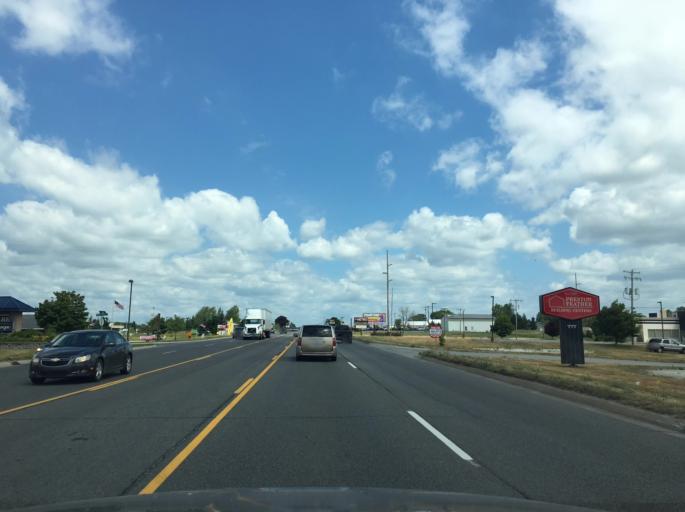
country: US
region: Michigan
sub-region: Grand Traverse County
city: Traverse City
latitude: 44.6774
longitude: -85.6563
